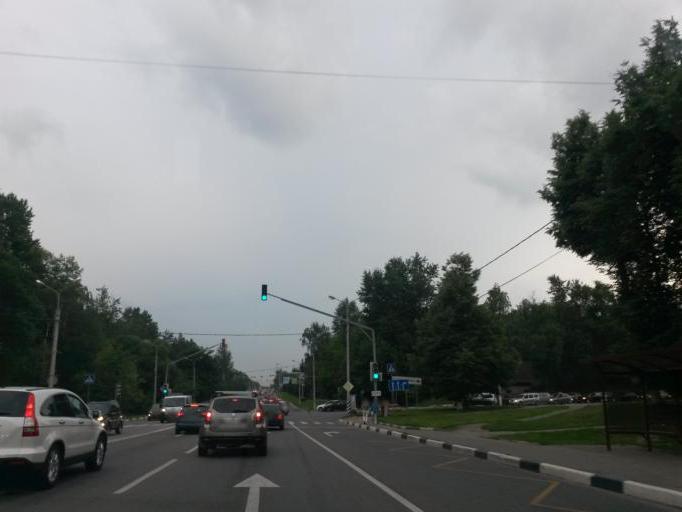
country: RU
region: Moskovskaya
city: Domodedovo
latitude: 55.4249
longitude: 37.7731
